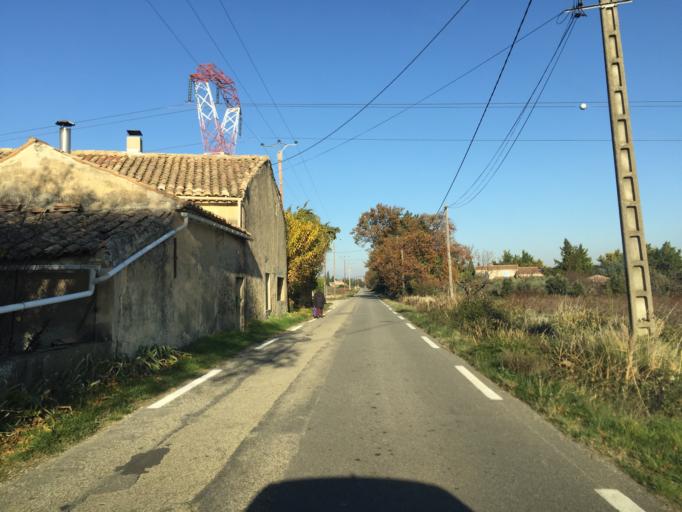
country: FR
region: Provence-Alpes-Cote d'Azur
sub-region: Departement du Vaucluse
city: Camaret-sur-Aigues
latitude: 44.1757
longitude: 4.8816
